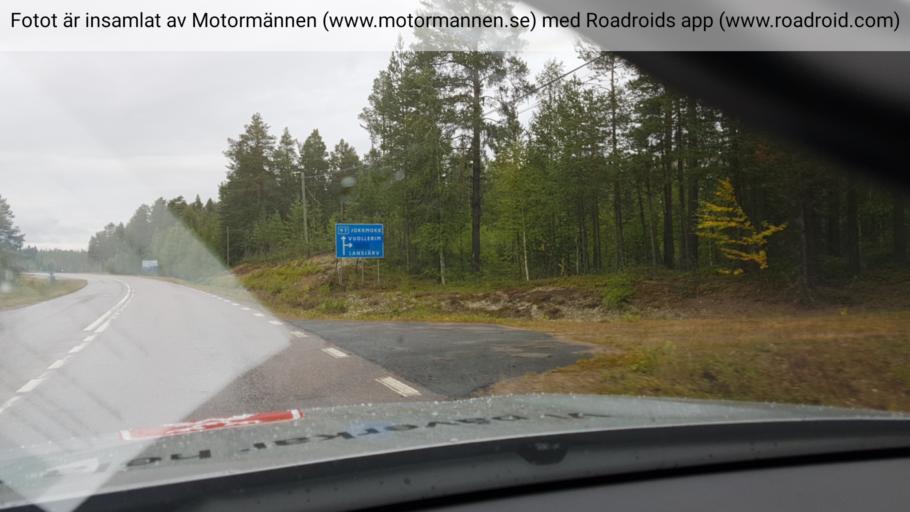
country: SE
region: Norrbotten
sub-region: Alvsbyns Kommun
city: AElvsbyn
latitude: 66.2274
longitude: 20.8750
